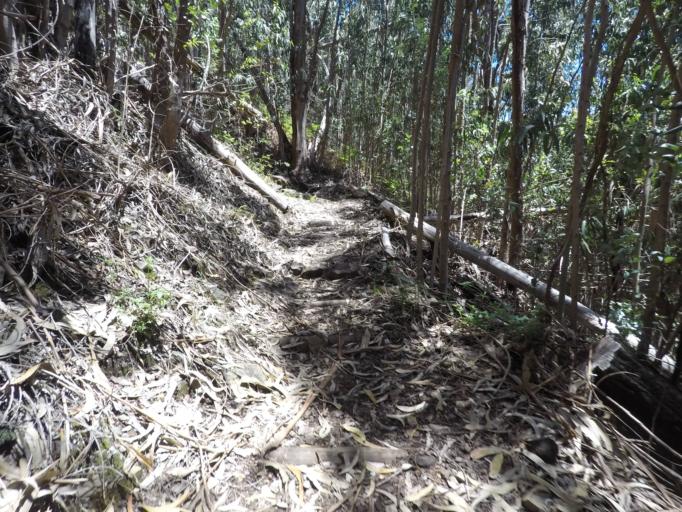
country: PT
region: Madeira
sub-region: Camara de Lobos
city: Curral das Freiras
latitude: 32.7483
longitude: -16.9696
